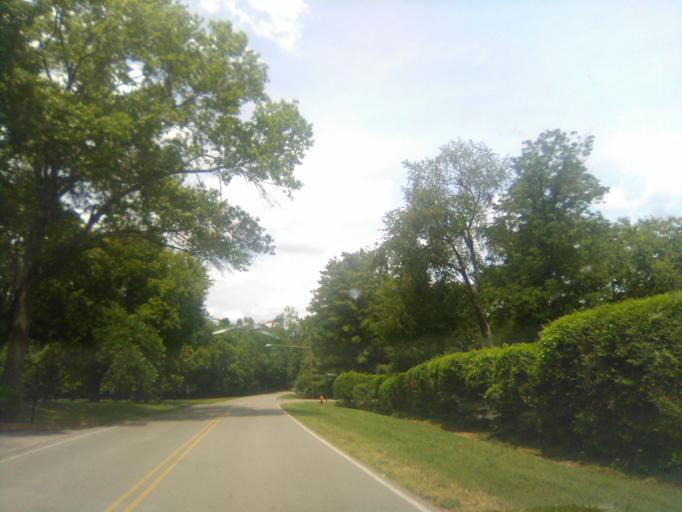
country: US
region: Tennessee
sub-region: Davidson County
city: Belle Meade
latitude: 36.0832
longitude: -86.8537
